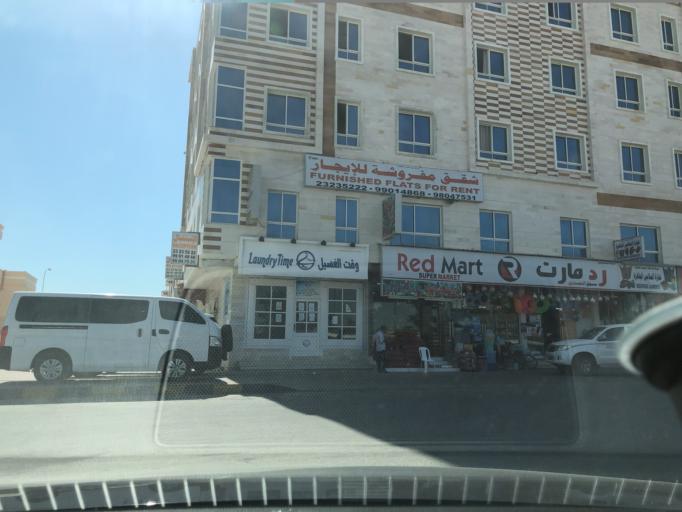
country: OM
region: Zufar
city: Salalah
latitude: 17.0258
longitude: 54.1579
